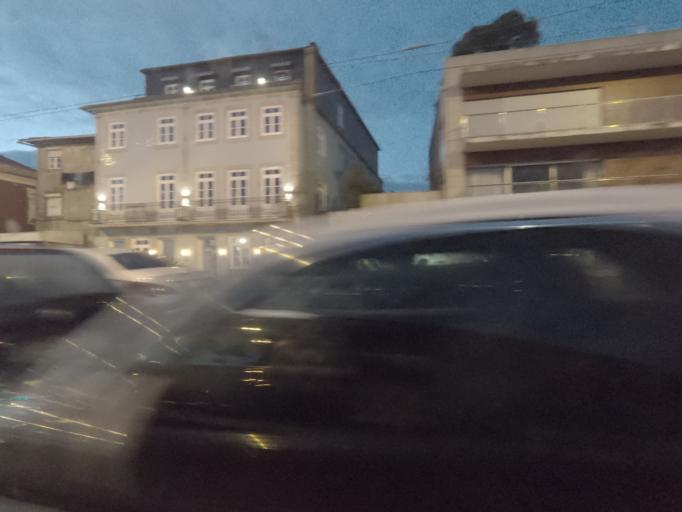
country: PT
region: Porto
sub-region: Vila Nova de Gaia
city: Canidelo
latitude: 41.1481
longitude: -8.6656
